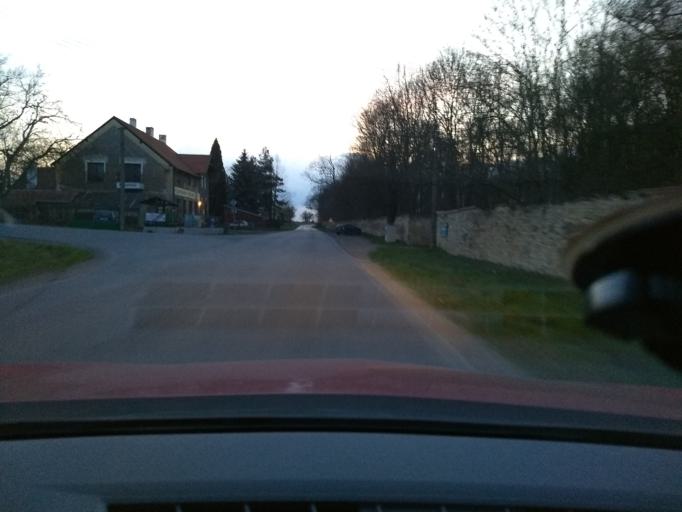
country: CZ
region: Central Bohemia
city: Jenec
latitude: 50.0682
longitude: 14.1866
